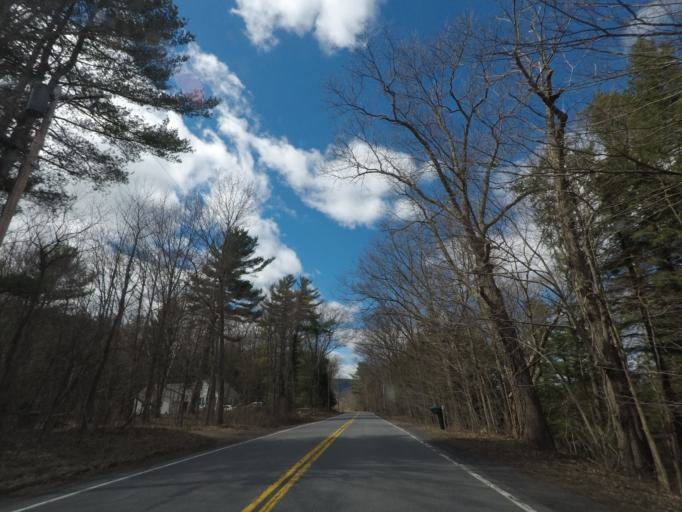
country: US
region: New York
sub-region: Albany County
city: Voorheesville
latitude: 42.6501
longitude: -73.9816
